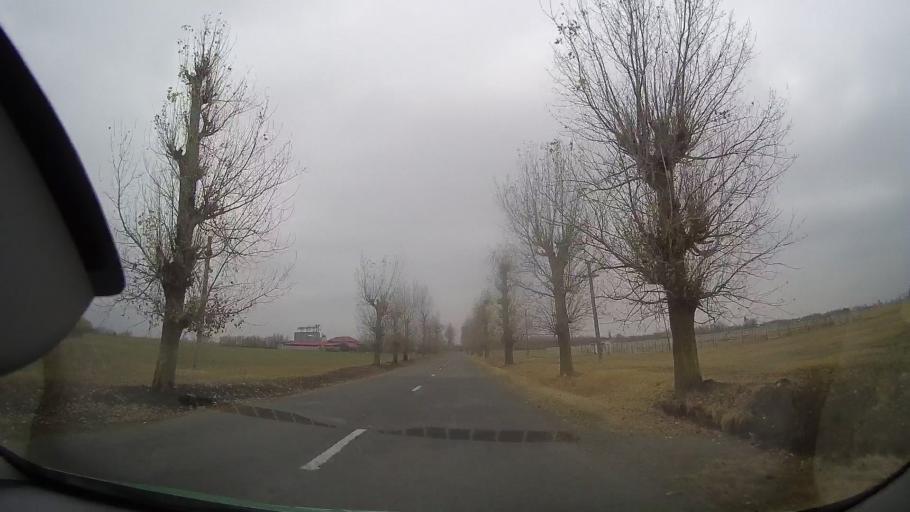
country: RO
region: Ialomita
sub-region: Comuna Grindu
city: Grindu
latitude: 44.7845
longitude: 26.9040
